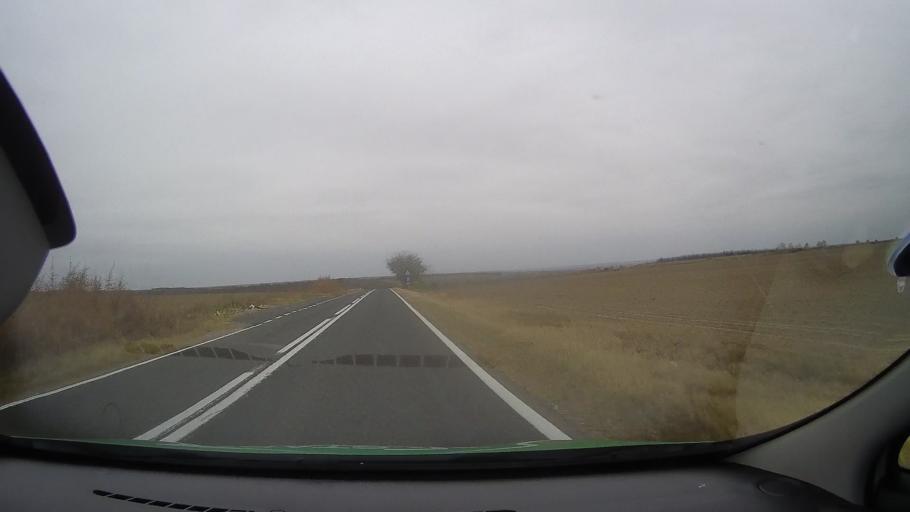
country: RO
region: Constanta
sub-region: Comuna Garliciu
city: Garliciu
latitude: 44.7107
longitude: 28.0835
